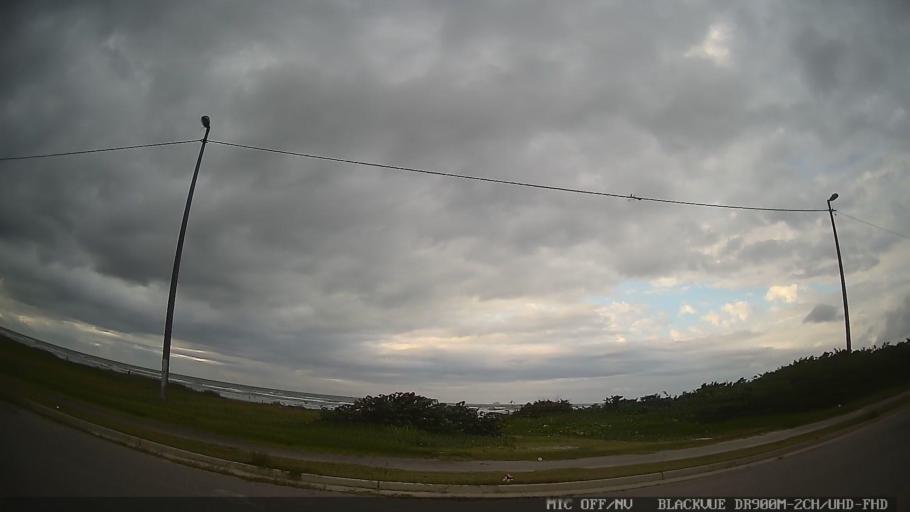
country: BR
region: Sao Paulo
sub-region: Itanhaem
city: Itanhaem
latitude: -24.2391
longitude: -46.8797
